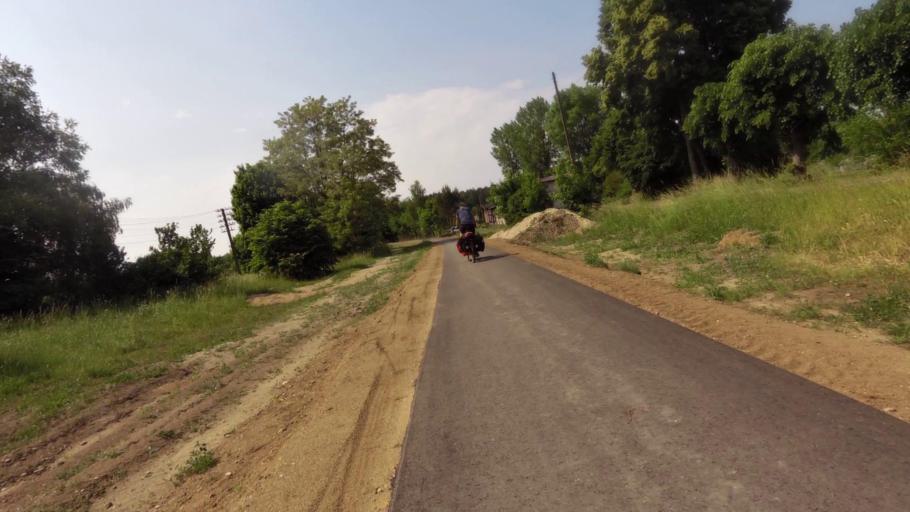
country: PL
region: West Pomeranian Voivodeship
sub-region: Powiat pyrzycki
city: Bielice
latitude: 53.2171
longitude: 14.6079
